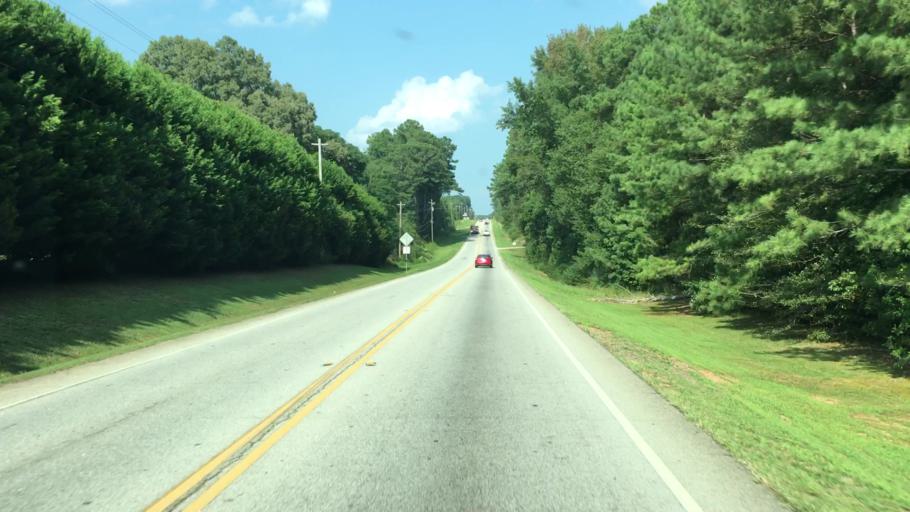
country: US
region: Georgia
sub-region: Walton County
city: Social Circle
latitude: 33.6258
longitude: -83.7410
